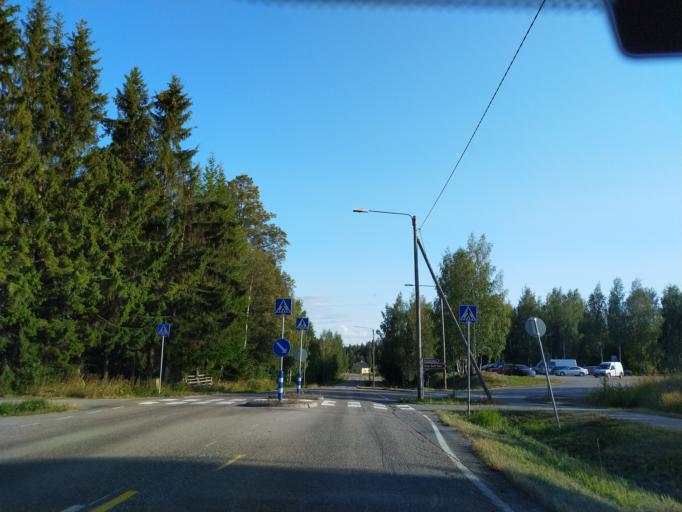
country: FI
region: Central Finland
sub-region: Jaemsae
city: Kuhmoinen
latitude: 61.5747
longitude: 25.1754
